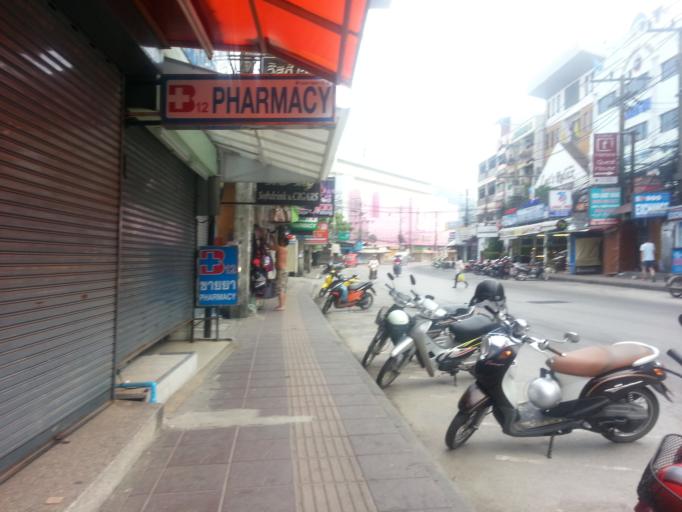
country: TH
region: Phuket
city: Patong
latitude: 7.8895
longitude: 98.2956
